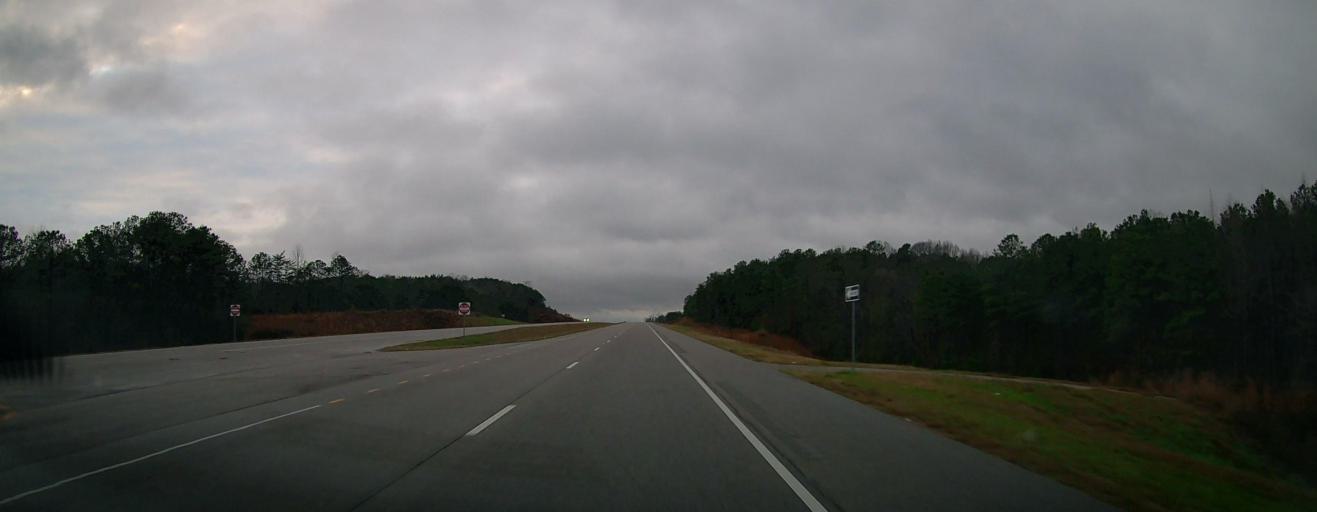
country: US
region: Alabama
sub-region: Bibb County
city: Centreville
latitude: 32.9507
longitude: -87.1058
